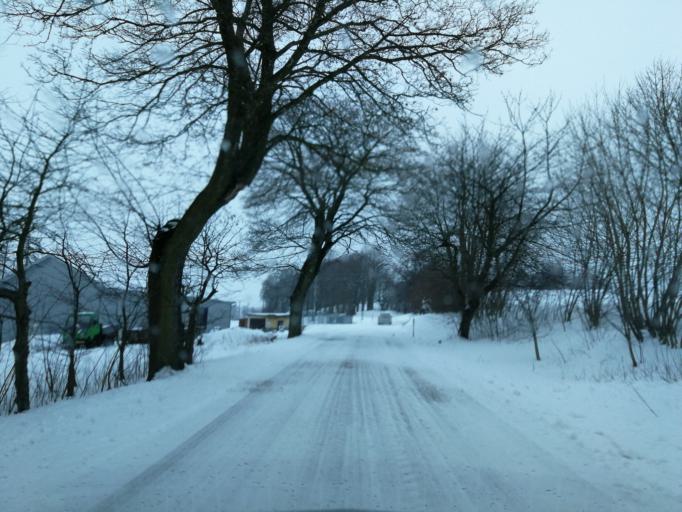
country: CZ
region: Vysocina
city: Heralec
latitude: 49.5281
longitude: 15.4705
